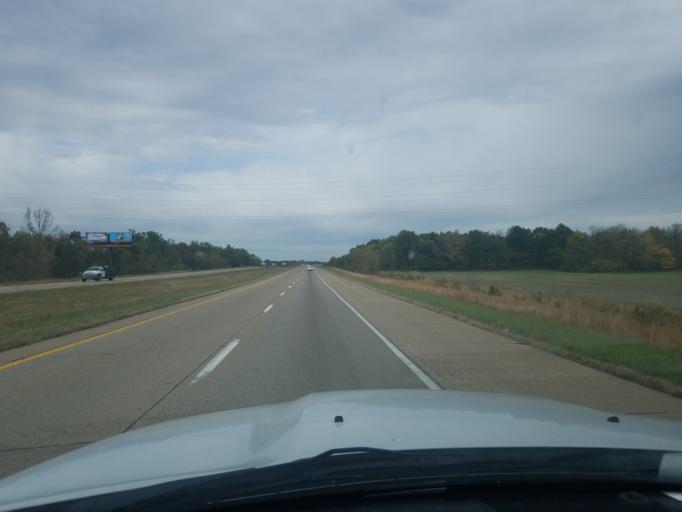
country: US
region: Indiana
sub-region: Vanderburgh County
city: Melody Hill
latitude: 38.0299
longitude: -87.4722
